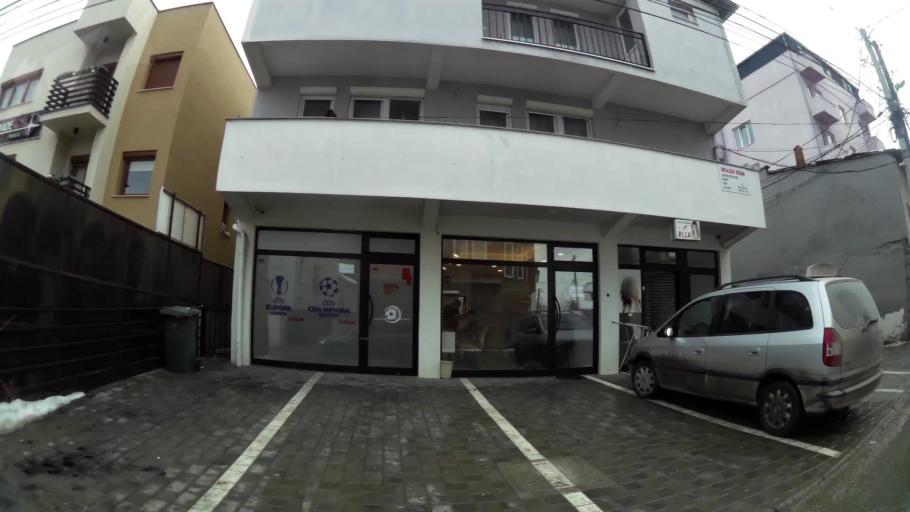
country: XK
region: Pristina
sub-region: Komuna e Prishtines
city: Pristina
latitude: 42.6602
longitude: 21.1827
